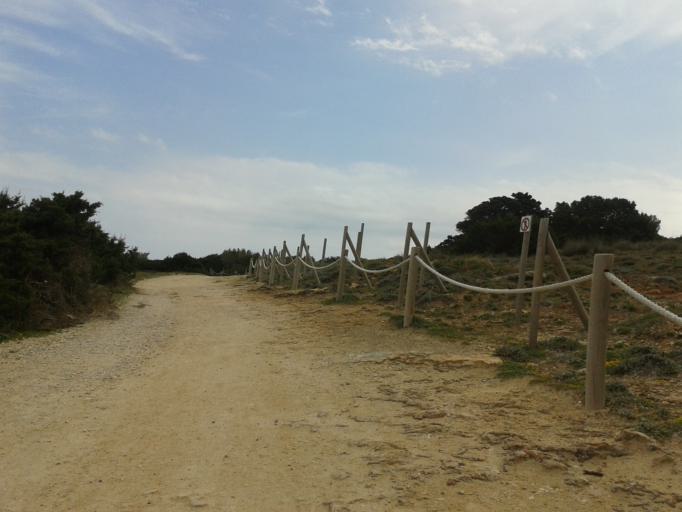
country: ES
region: Balearic Islands
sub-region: Illes Balears
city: Son Servera
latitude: 39.5855
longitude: 3.3902
